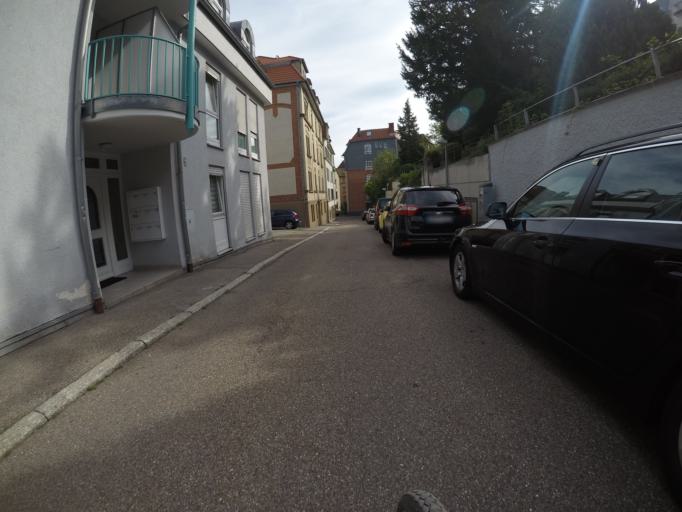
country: DE
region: Baden-Wuerttemberg
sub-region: Regierungsbezirk Stuttgart
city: Stuttgart
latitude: 48.7583
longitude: 9.1535
